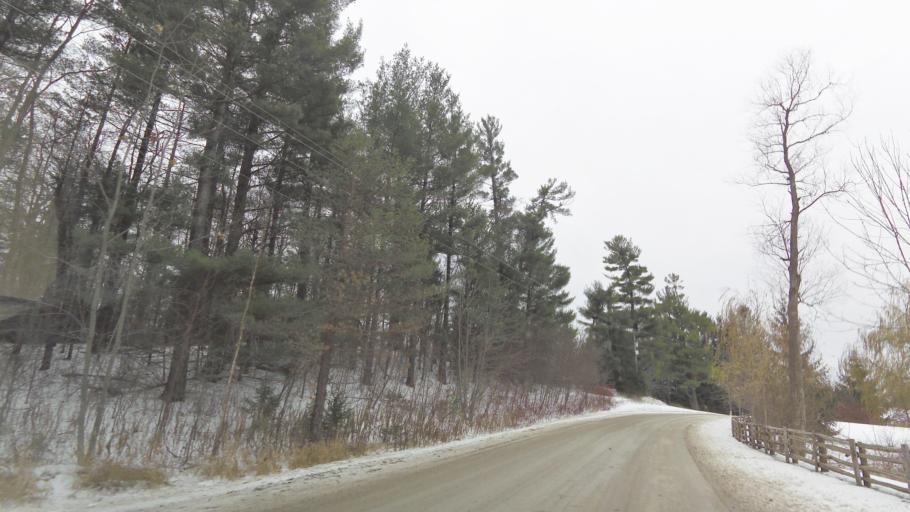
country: CA
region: Ontario
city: Vaughan
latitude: 43.9484
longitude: -79.6185
